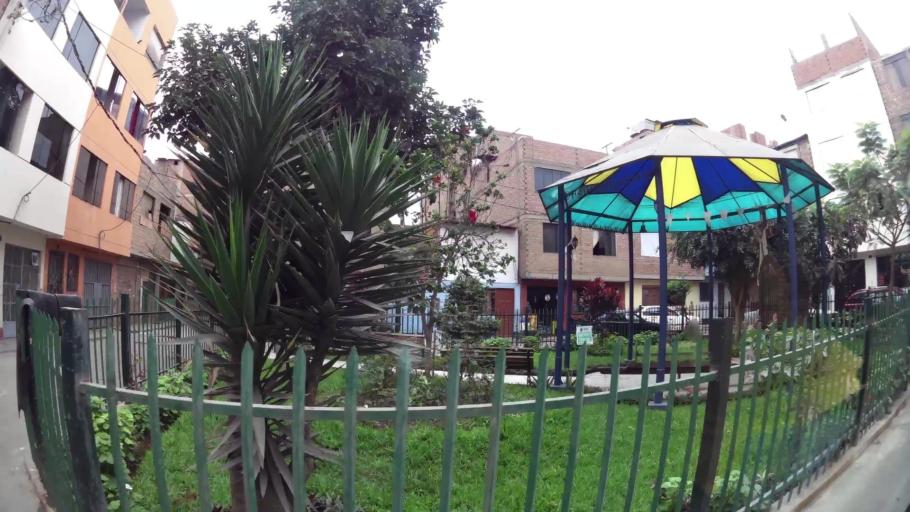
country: PE
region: Lima
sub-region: Lima
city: Surco
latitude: -12.1151
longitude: -77.0145
